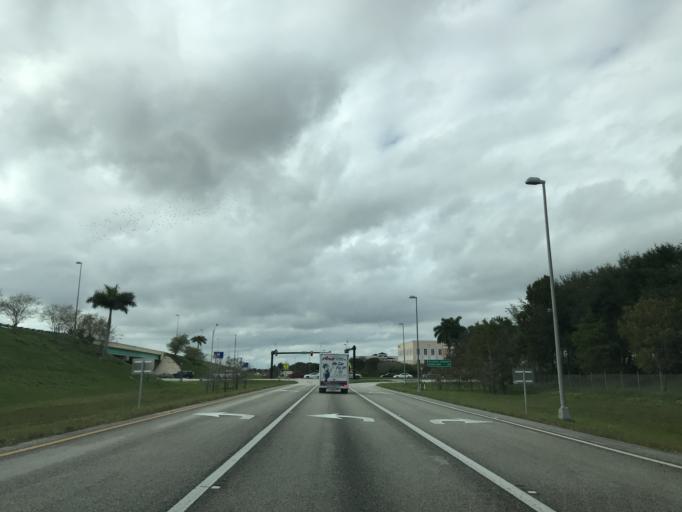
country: US
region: Florida
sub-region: Broward County
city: Coral Springs
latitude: 26.3028
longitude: -80.2775
